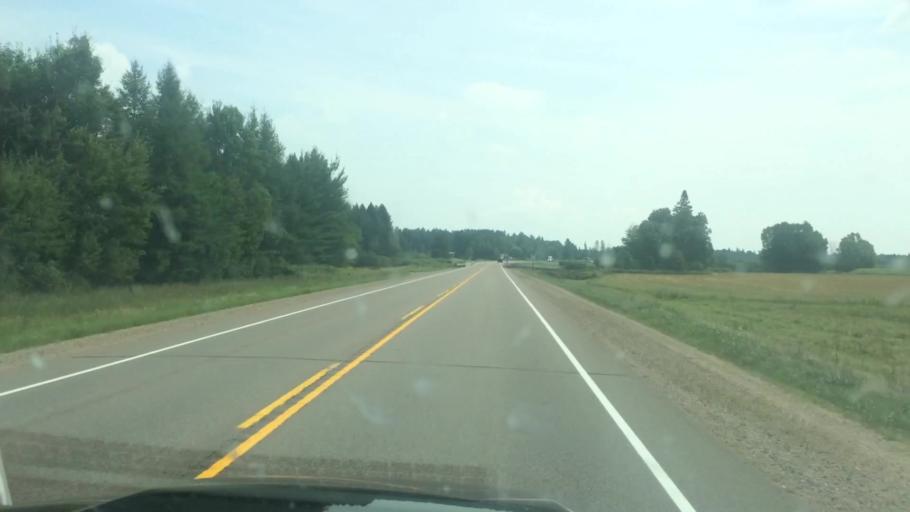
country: US
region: Wisconsin
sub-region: Langlade County
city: Antigo
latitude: 45.1461
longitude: -89.2838
